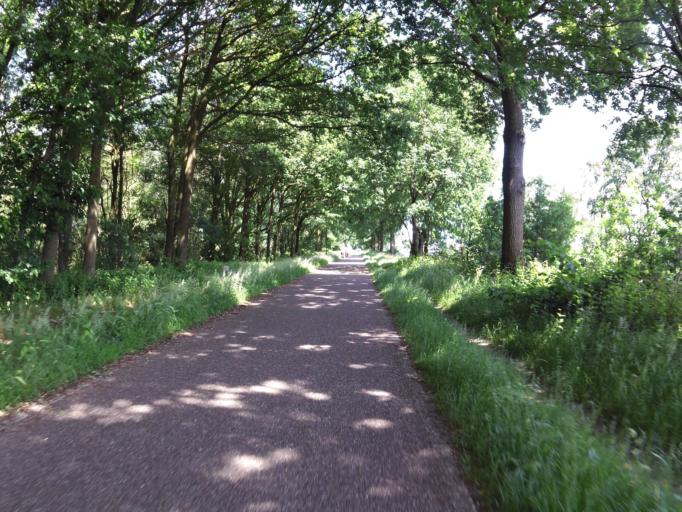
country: NL
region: North Brabant
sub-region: Gemeente Son en Breugel
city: Son
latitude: 51.5050
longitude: 5.4783
